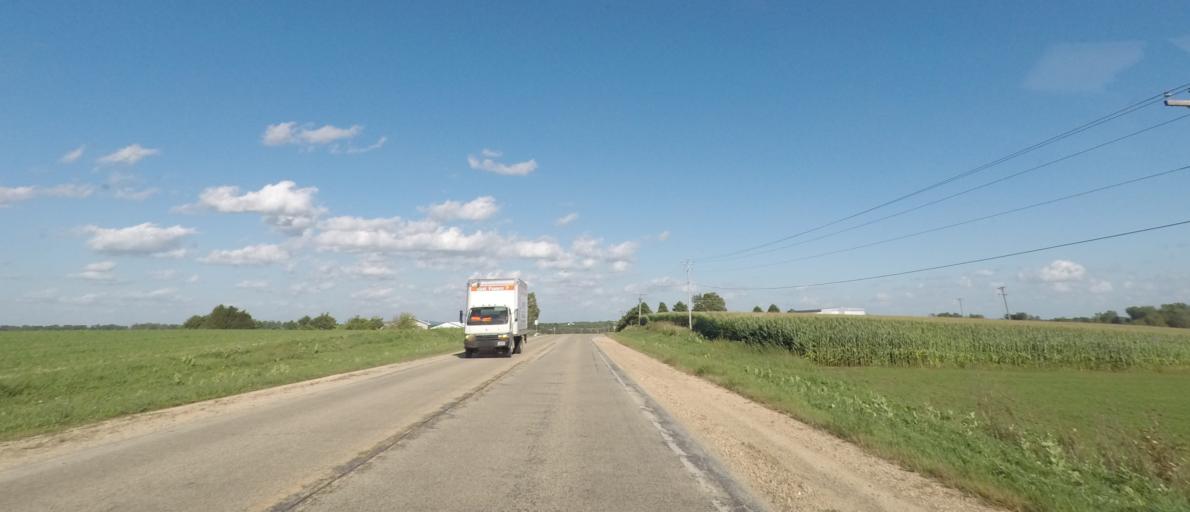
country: US
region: Wisconsin
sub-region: Iowa County
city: Dodgeville
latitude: 42.9817
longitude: -90.0950
